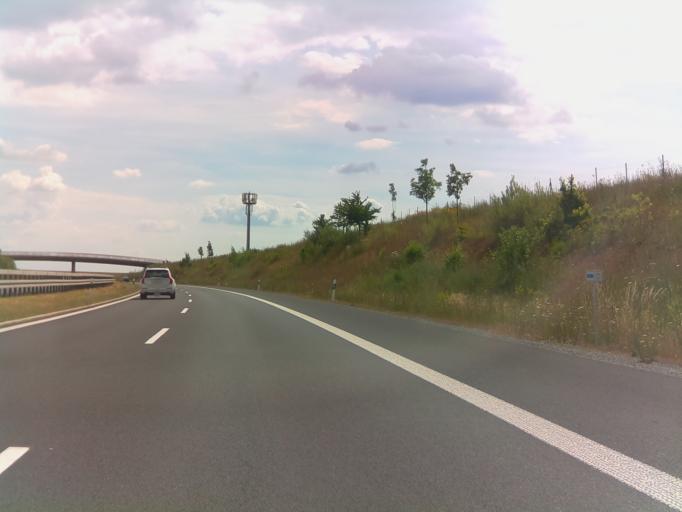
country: DE
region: Bavaria
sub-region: Regierungsbezirk Unterfranken
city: Geldersheim
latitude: 50.0447
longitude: 10.1402
